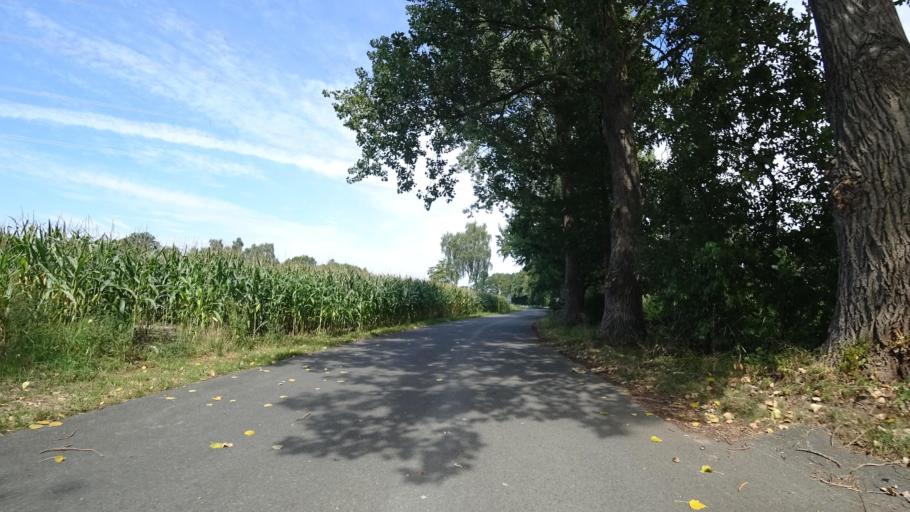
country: DE
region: North Rhine-Westphalia
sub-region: Regierungsbezirk Detmold
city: Guetersloh
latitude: 51.9470
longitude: 8.3836
